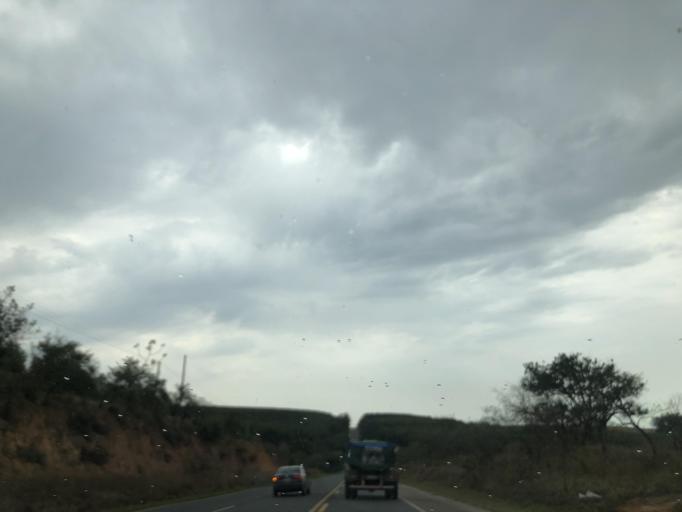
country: BR
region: Sao Paulo
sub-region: Salto De Pirapora
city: Salto de Pirapora
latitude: -23.6822
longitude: -47.6055
